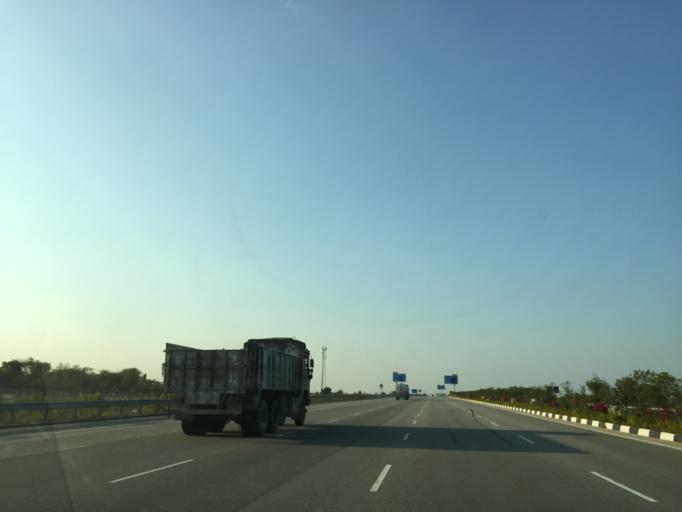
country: IN
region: Telangana
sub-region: Rangareddi
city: Ghatkesar
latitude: 17.5084
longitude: 78.6523
